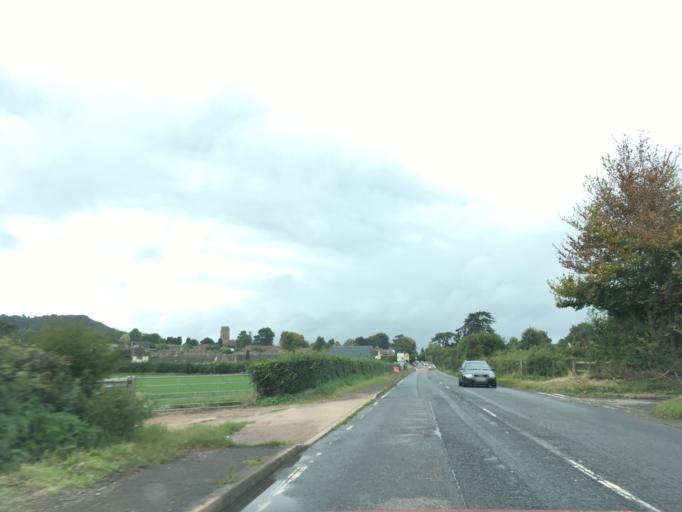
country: GB
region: England
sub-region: Herefordshire
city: Lea
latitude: 51.9050
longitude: -2.5289
